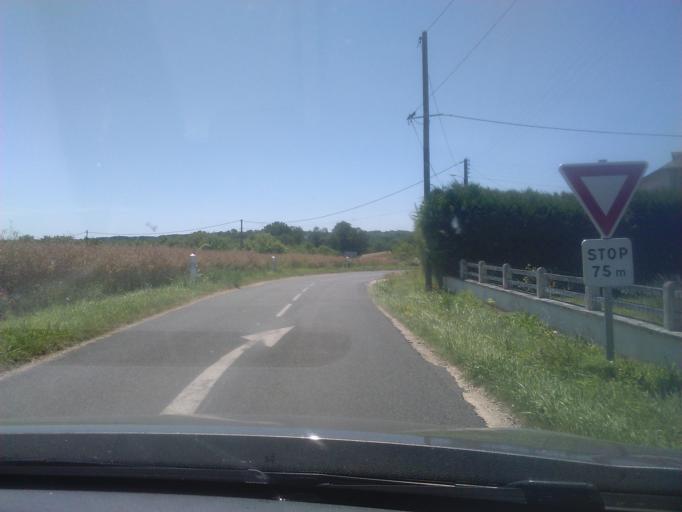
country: FR
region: Centre
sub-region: Departement du Loir-et-Cher
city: Saint-Sulpice-de-Pommeray
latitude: 47.5974
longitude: 1.2120
